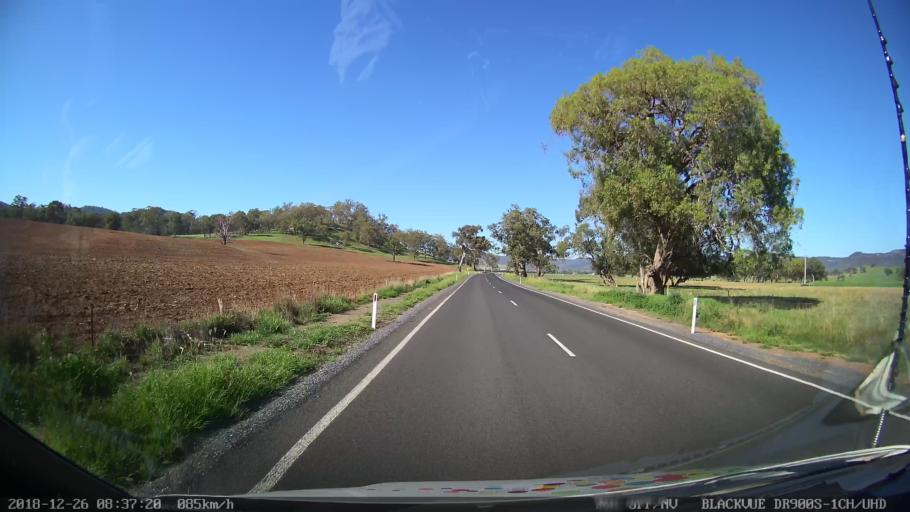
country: AU
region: New South Wales
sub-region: Upper Hunter Shire
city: Merriwa
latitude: -32.4313
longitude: 150.0911
